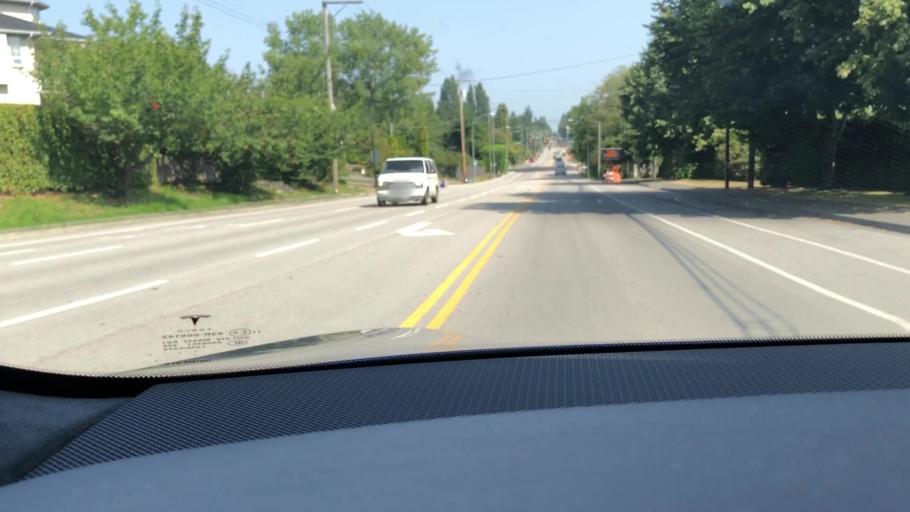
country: US
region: Washington
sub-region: Whatcom County
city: Point Roberts
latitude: 49.0082
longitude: -123.0687
